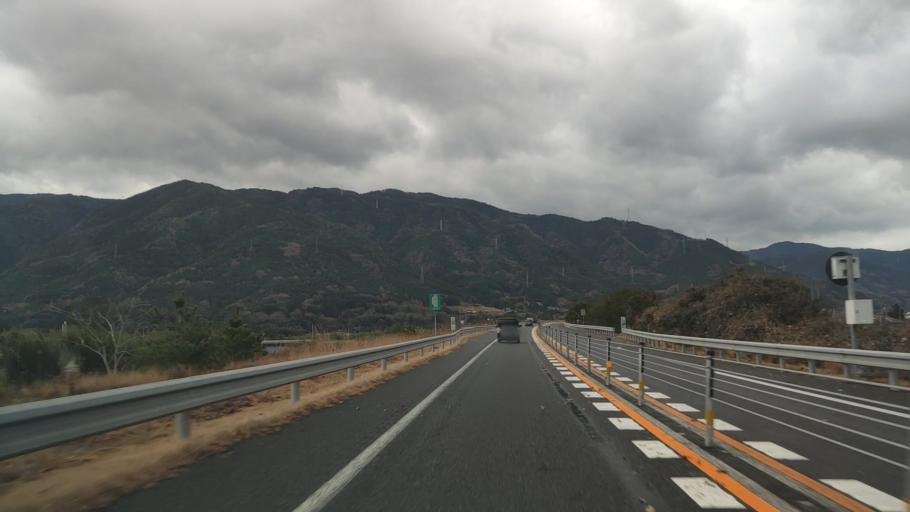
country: JP
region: Tokushima
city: Ikedacho
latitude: 34.0435
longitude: 133.9114
